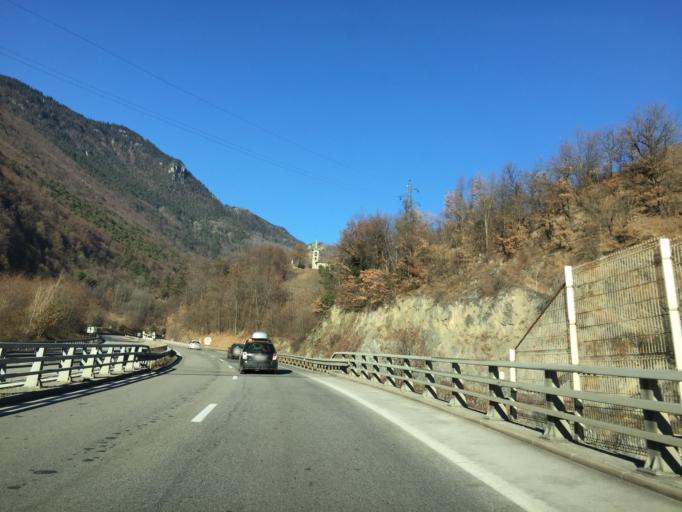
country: FR
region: Rhone-Alpes
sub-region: Departement de la Savoie
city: Moutiers
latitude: 45.5083
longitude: 6.5651
